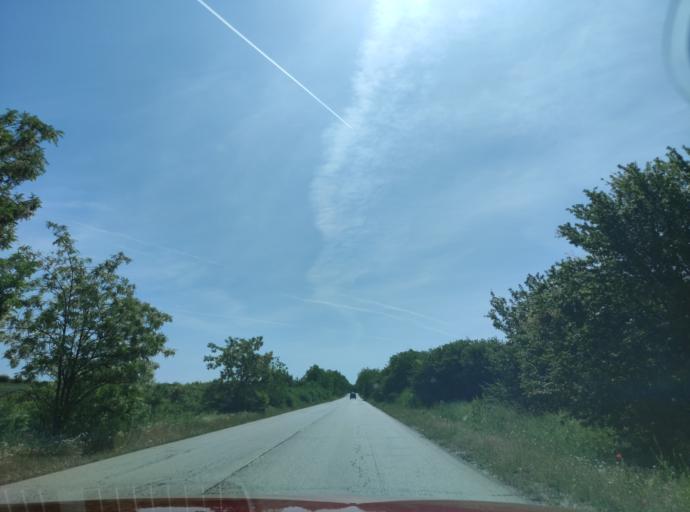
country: BG
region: Pleven
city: Iskur
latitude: 43.4492
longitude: 24.3199
